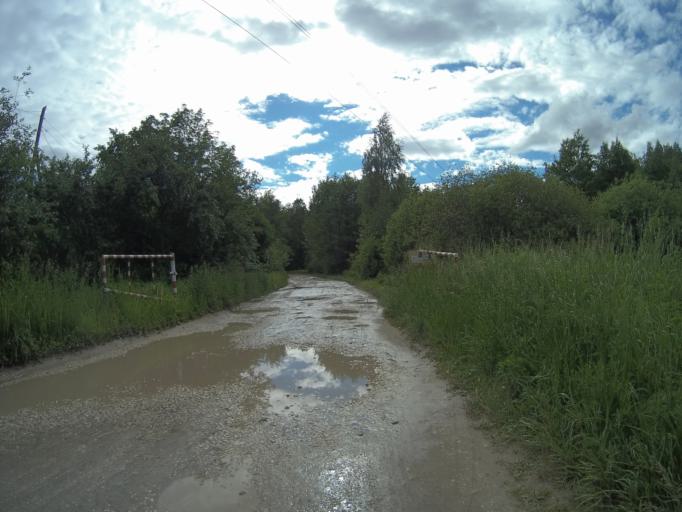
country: RU
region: Vladimir
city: Bogolyubovo
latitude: 56.1065
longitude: 40.5562
